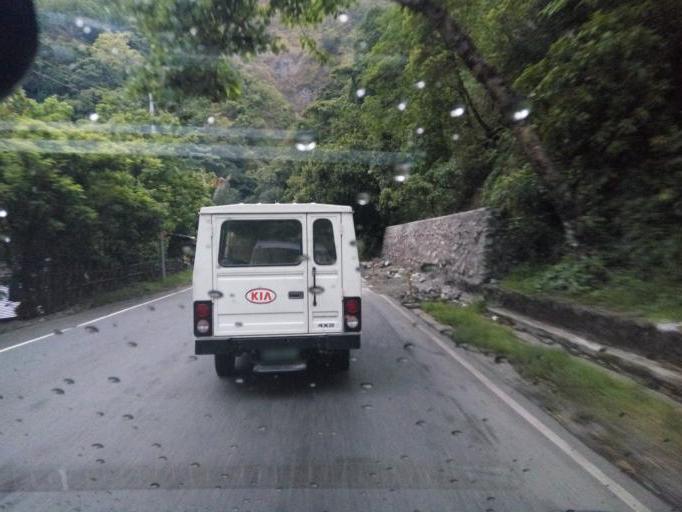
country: PH
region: Cagayan Valley
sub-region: Province of Nueva Vizcaya
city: Santa Fe
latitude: 16.1174
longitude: 120.9283
